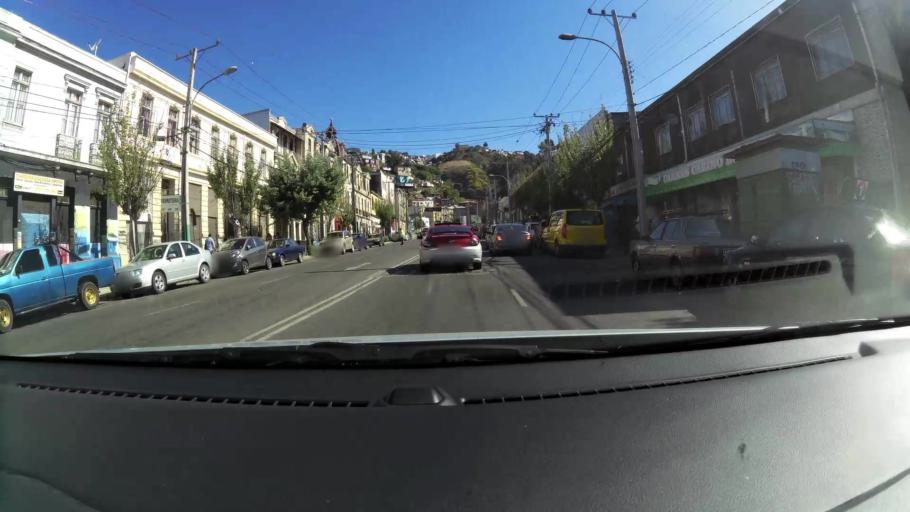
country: CL
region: Valparaiso
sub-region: Provincia de Valparaiso
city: Valparaiso
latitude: -33.0500
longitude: -71.6130
